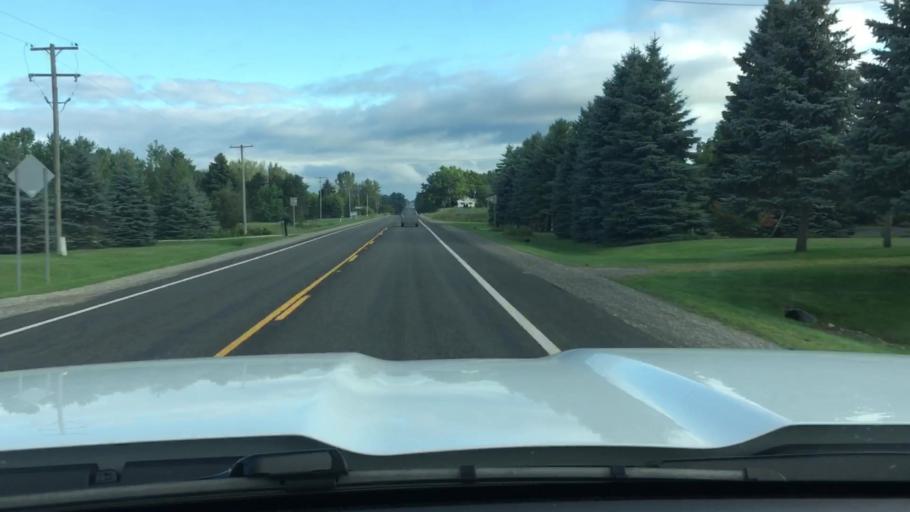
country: US
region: Michigan
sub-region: Tuscola County
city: Caro
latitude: 43.3512
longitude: -83.3826
